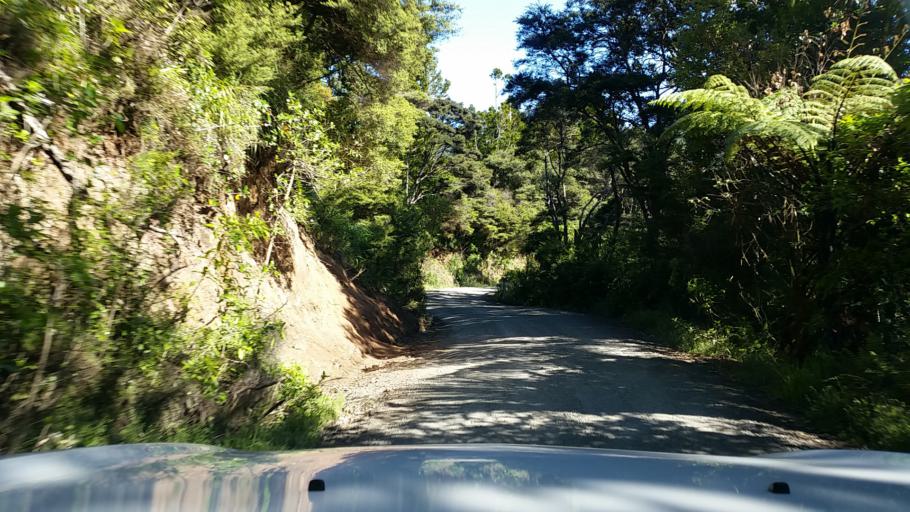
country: NZ
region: Auckland
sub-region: Auckland
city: Titirangi
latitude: -37.0313
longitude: 174.5216
